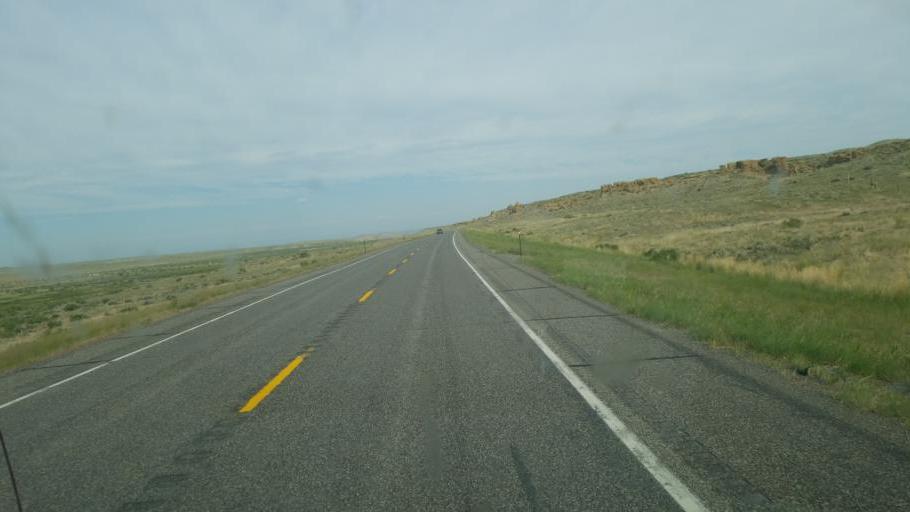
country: US
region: Wyoming
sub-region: Fremont County
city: Riverton
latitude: 43.2209
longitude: -108.0162
